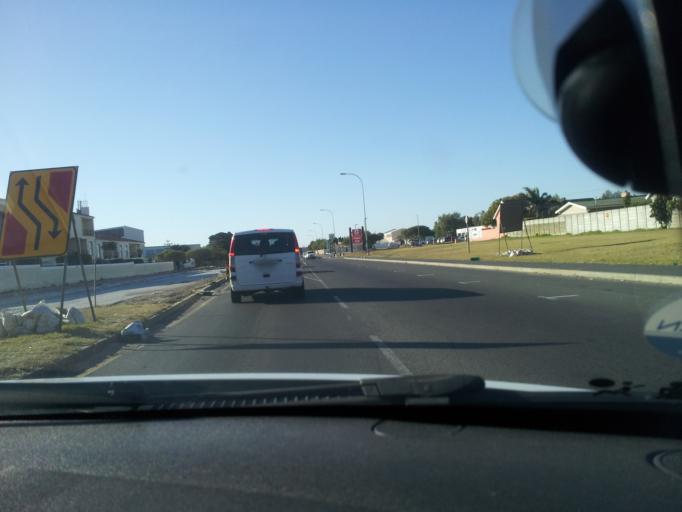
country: ZA
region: Western Cape
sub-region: Cape Winelands District Municipality
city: Stellenbosch
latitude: -34.1022
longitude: 18.8317
